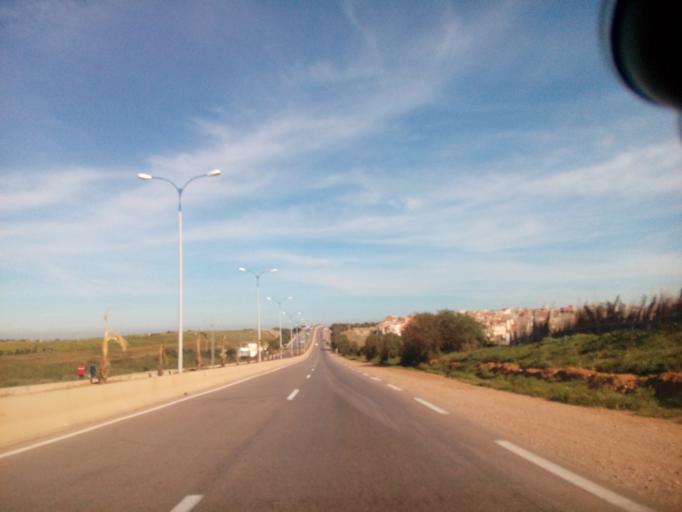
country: DZ
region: Mostaganem
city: Mostaganem
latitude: 35.8269
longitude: -0.0118
